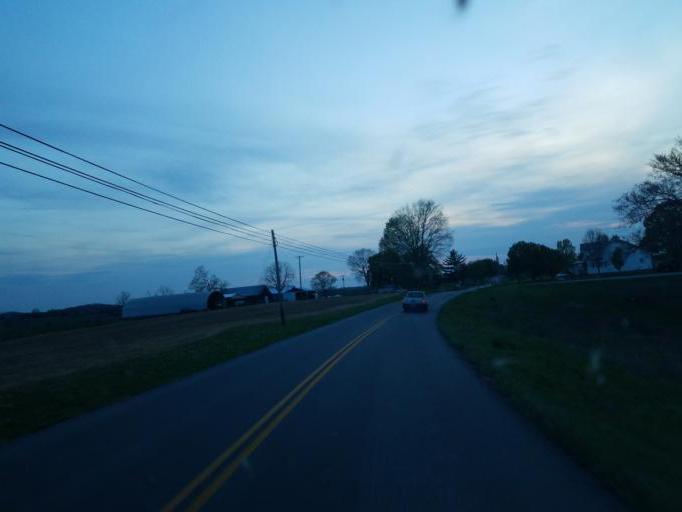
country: US
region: Kentucky
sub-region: Hart County
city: Munfordville
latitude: 37.2730
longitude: -85.8333
